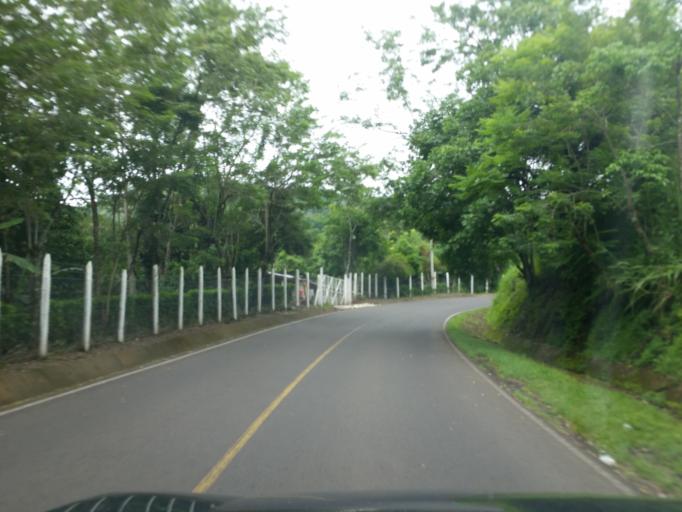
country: NI
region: Matagalpa
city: San Ramon
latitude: 12.9964
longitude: -85.8174
